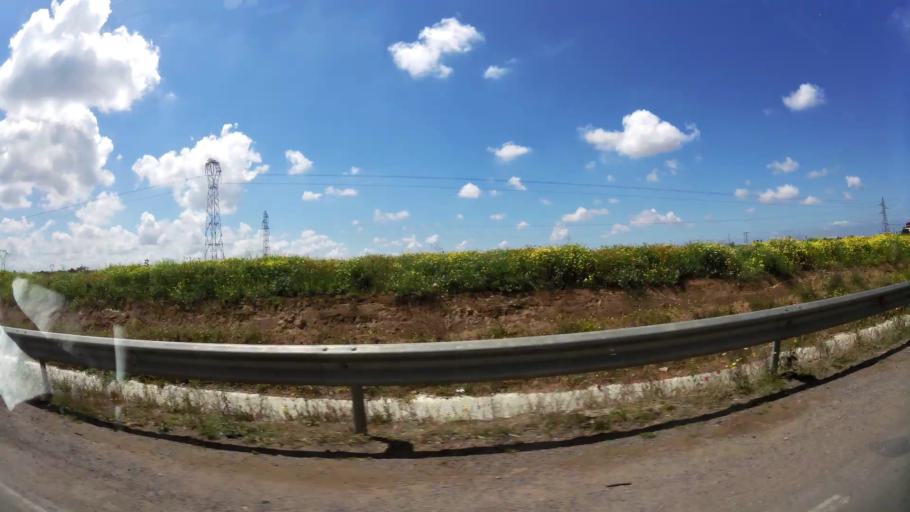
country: MA
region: Grand Casablanca
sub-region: Casablanca
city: Casablanca
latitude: 33.5158
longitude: -7.6144
